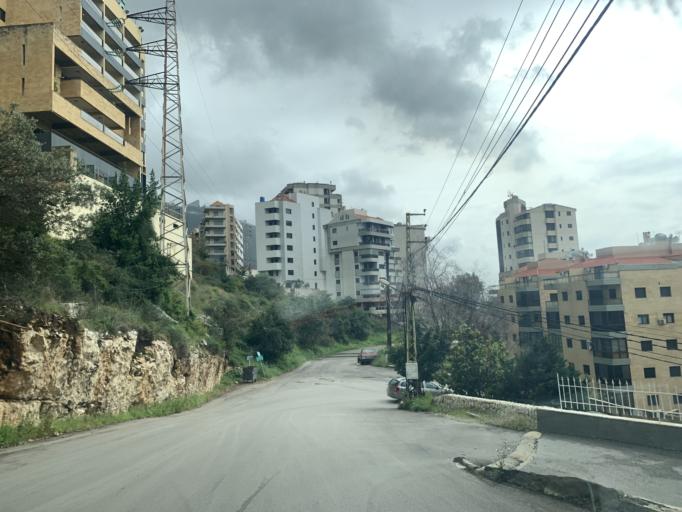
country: LB
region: Mont-Liban
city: Djounie
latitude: 34.0028
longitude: 35.6519
